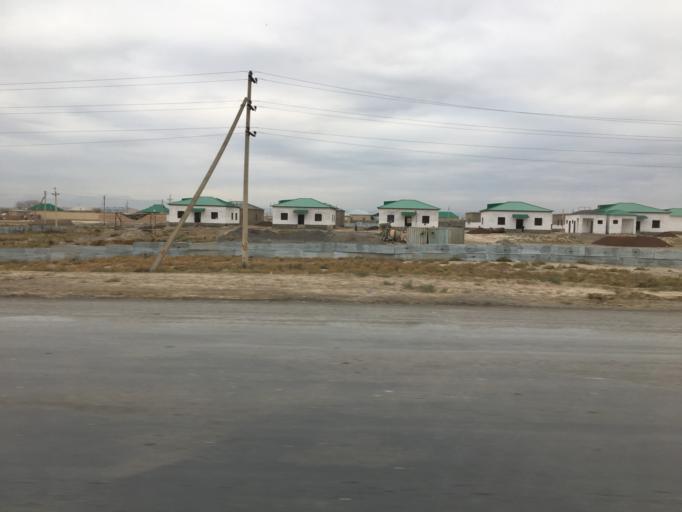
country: TM
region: Ahal
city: Kaka
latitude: 37.3570
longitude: 59.6376
